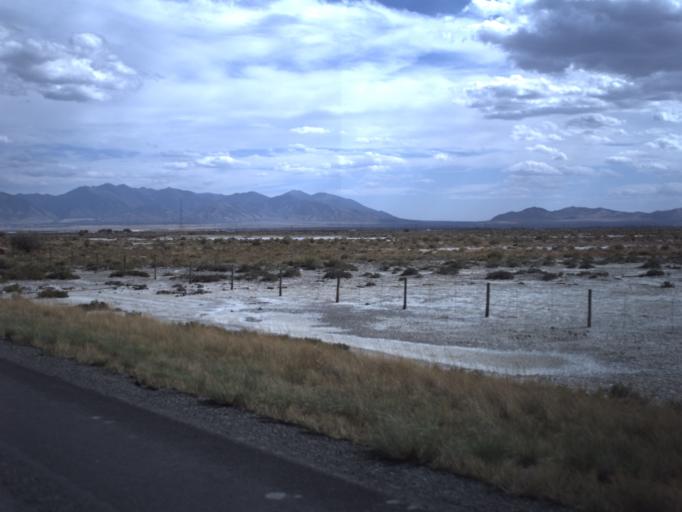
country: US
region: Utah
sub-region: Tooele County
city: Grantsville
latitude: 40.6944
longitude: -112.4726
